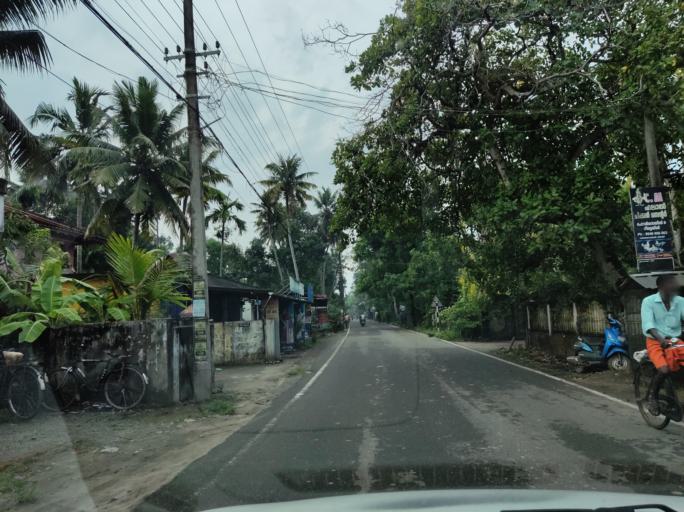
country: IN
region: Kerala
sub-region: Alappuzha
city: Kayankulam
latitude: 9.2434
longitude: 76.4534
